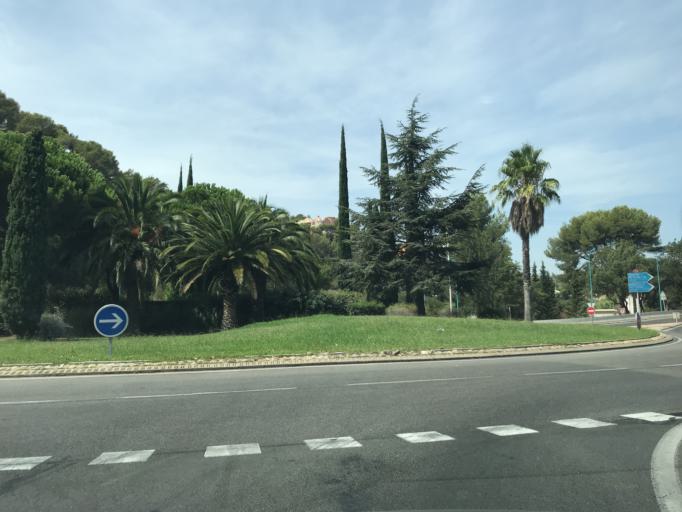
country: FR
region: Provence-Alpes-Cote d'Azur
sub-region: Departement du Var
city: Bandol
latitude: 43.1421
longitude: 5.7689
